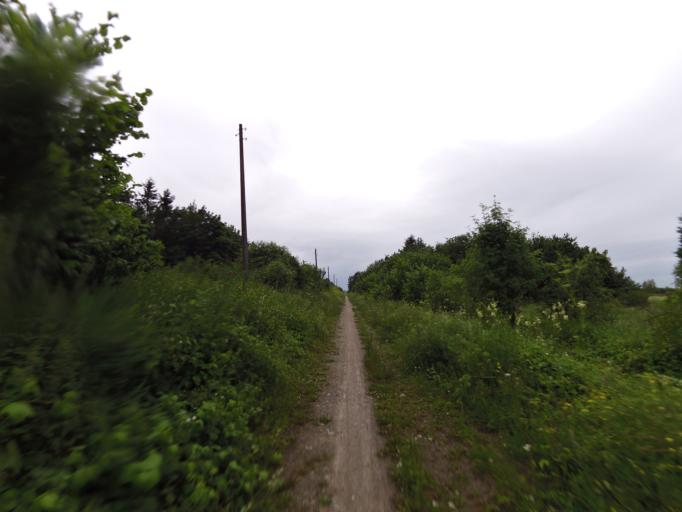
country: EE
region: Laeaene
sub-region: Ridala Parish
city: Uuemoisa
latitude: 58.9528
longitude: 23.8008
